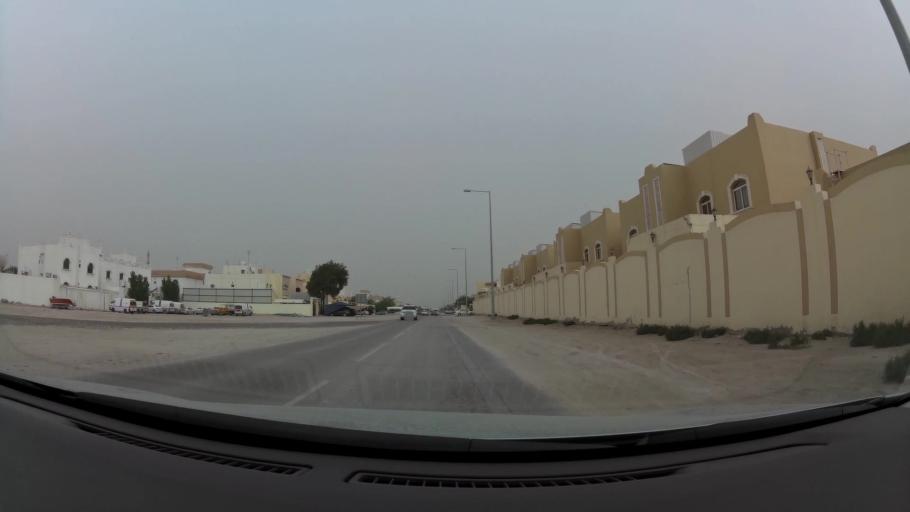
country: QA
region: Baladiyat ad Dawhah
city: Doha
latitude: 25.2520
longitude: 51.4941
